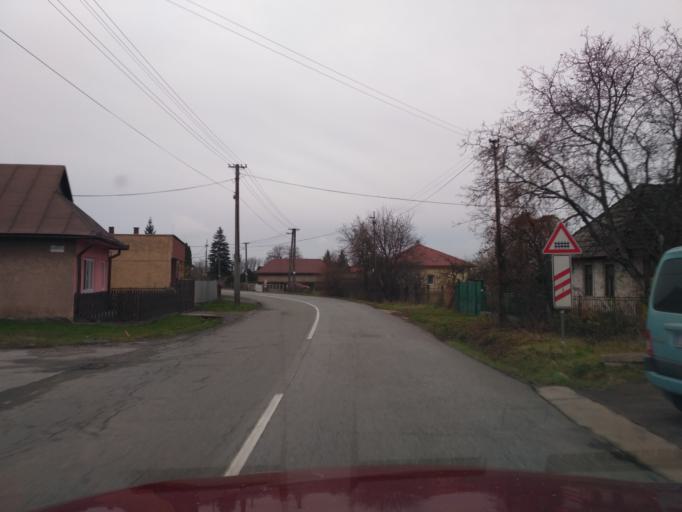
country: SK
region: Kosicky
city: Kosice
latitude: 48.5912
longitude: 21.1681
